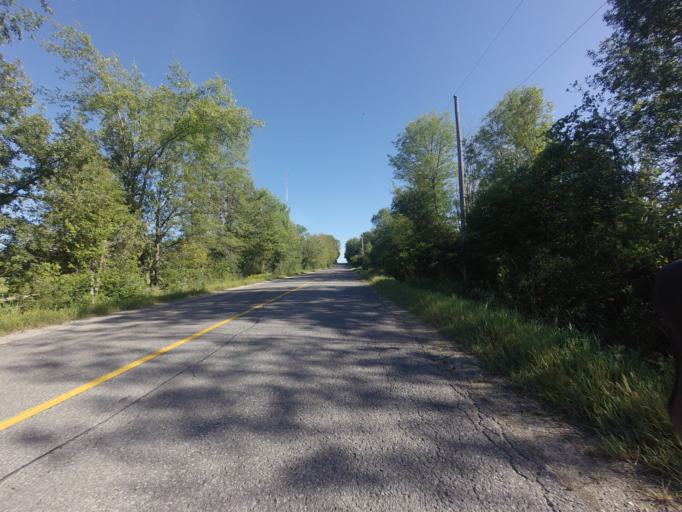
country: CA
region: Ontario
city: Perth
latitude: 44.9242
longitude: -76.3611
